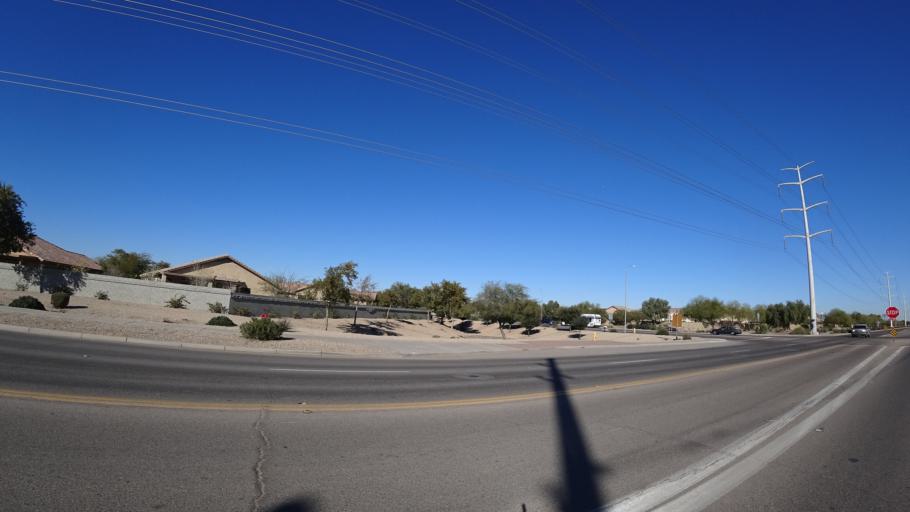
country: US
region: Arizona
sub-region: Maricopa County
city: Tolleson
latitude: 33.4084
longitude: -112.2222
